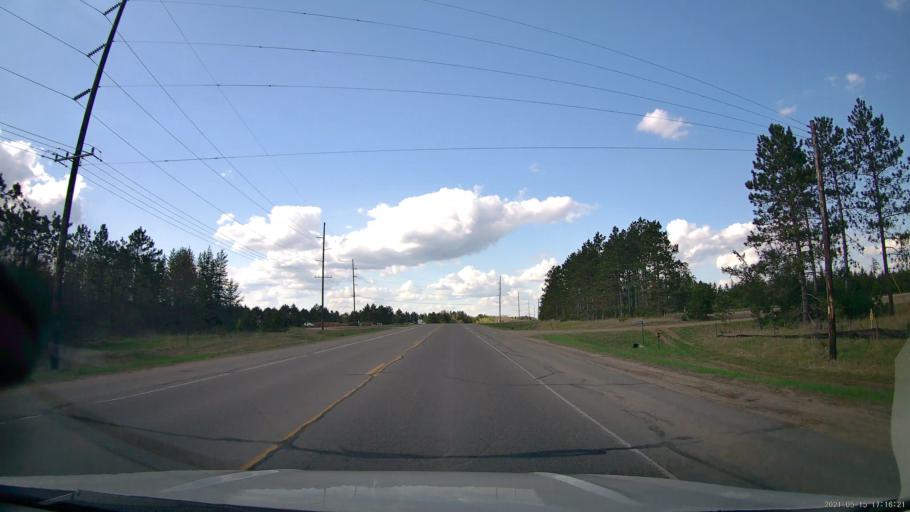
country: US
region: Minnesota
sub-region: Hubbard County
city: Park Rapids
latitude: 46.9278
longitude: -95.0161
